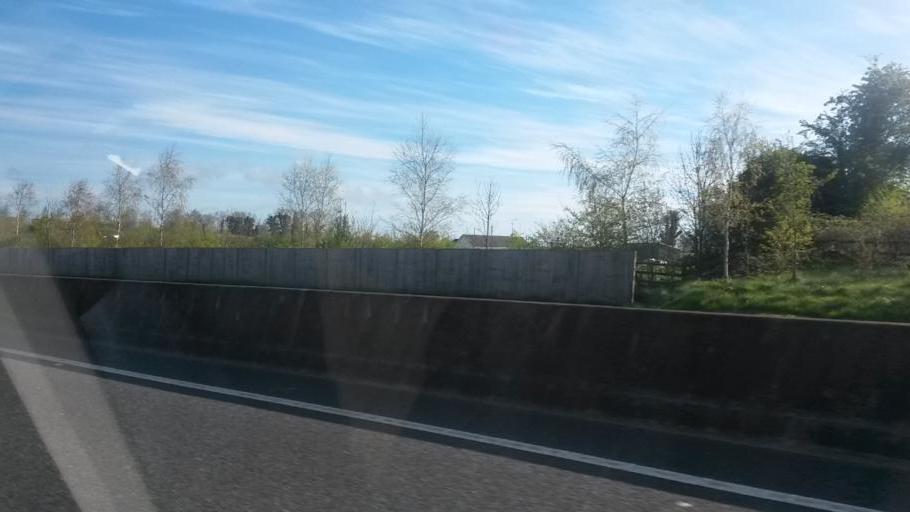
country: IE
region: Leinster
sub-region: An Mhi
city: Navan
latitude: 53.6617
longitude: -6.7580
